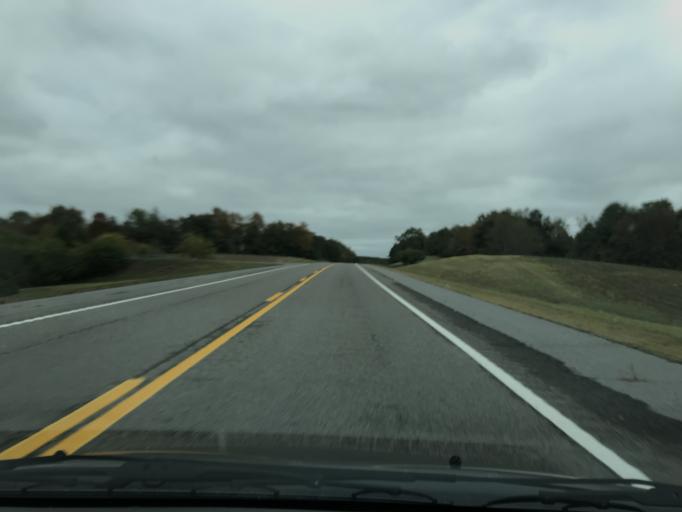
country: US
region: Tennessee
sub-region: Rhea County
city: Graysville
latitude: 35.4304
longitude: -85.0250
